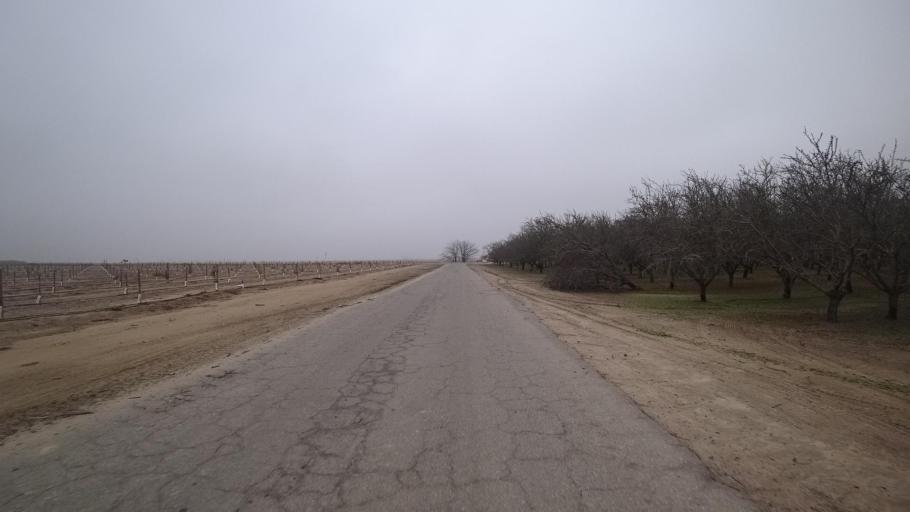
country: US
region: California
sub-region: Kern County
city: Lost Hills
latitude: 35.5732
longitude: -119.5362
